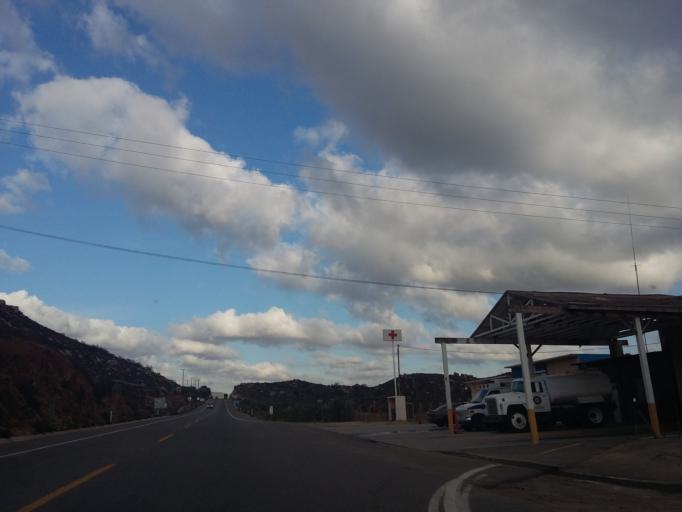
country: MX
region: Baja California
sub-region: Ensenada
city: Rancho Verde
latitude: 32.1053
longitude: -116.5577
